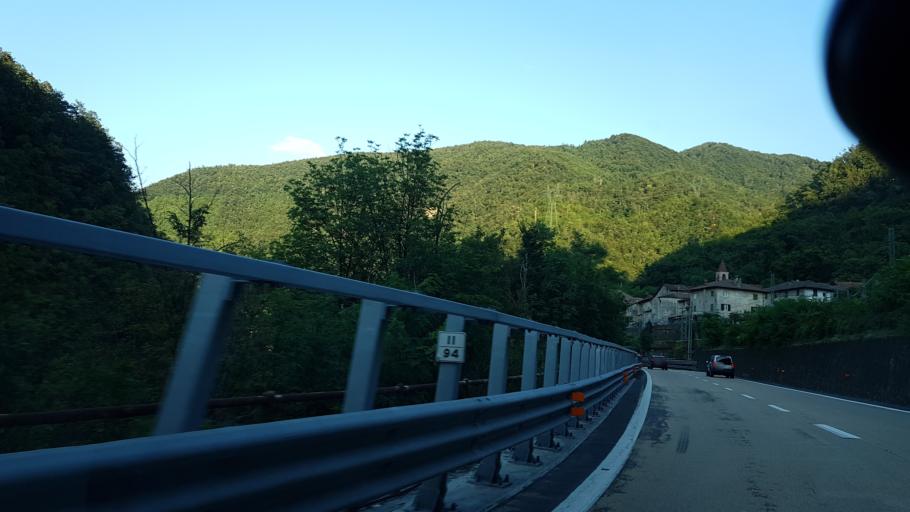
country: IT
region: Liguria
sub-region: Provincia di Genova
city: Isola del Cantone
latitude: 44.6589
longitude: 8.9194
